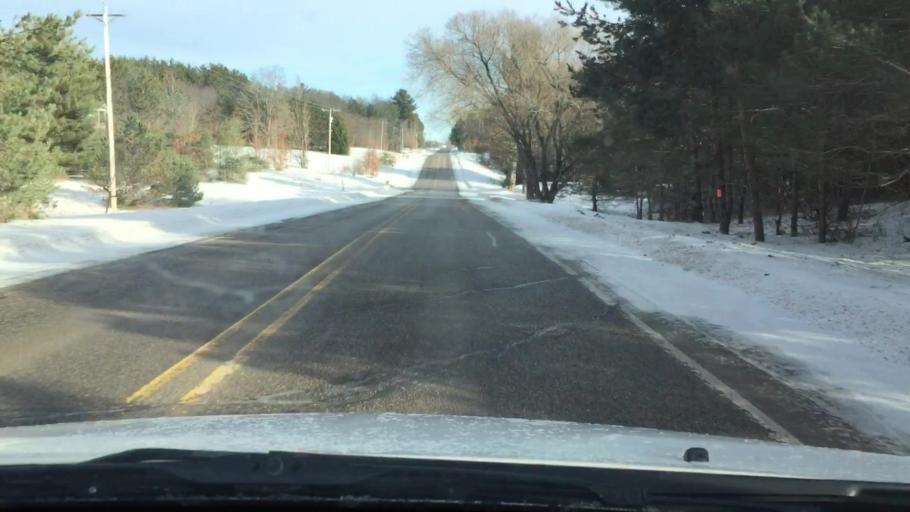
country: US
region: Michigan
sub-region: Kalkaska County
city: Kalkaska
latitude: 44.6408
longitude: -85.2359
